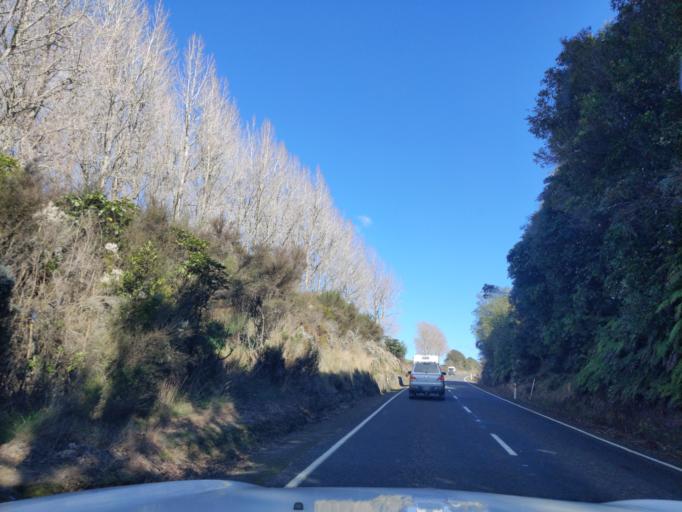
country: NZ
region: Waikato
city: Turangi
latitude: -38.7156
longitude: 175.6610
